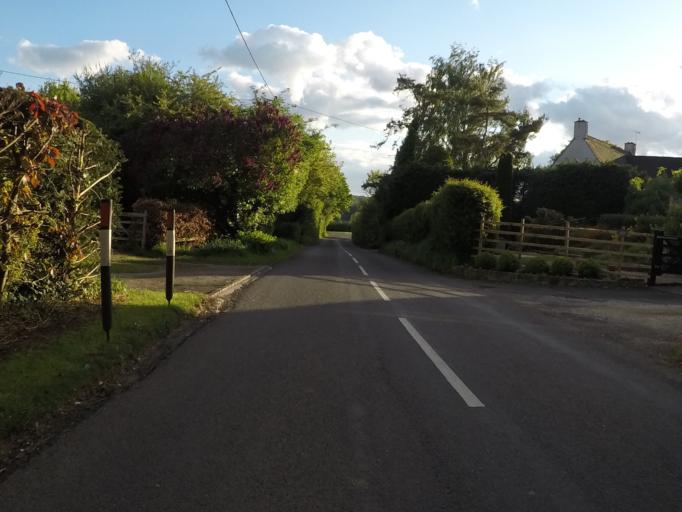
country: GB
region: England
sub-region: Oxfordshire
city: Charlbury
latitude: 51.8667
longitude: -1.4731
